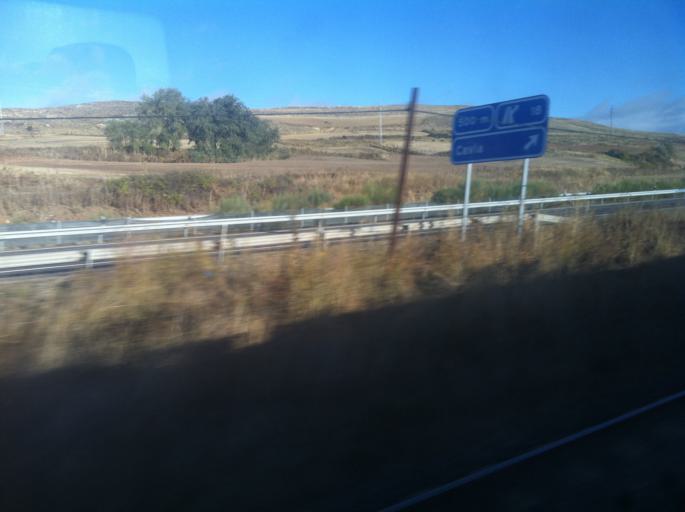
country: ES
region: Castille and Leon
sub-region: Provincia de Burgos
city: Estepar
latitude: 42.2836
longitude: -3.8673
